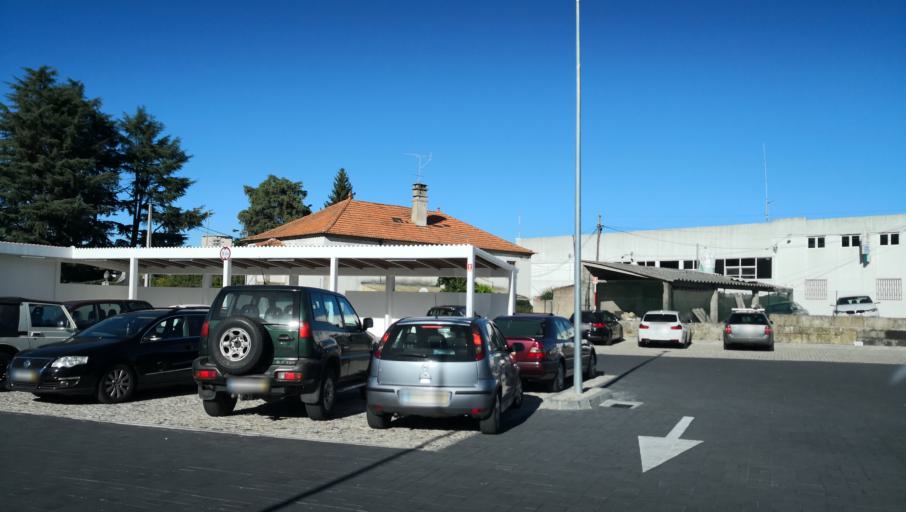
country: PT
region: Vila Real
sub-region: Vila Real
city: Vila Real
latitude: 41.3083
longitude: -7.7348
